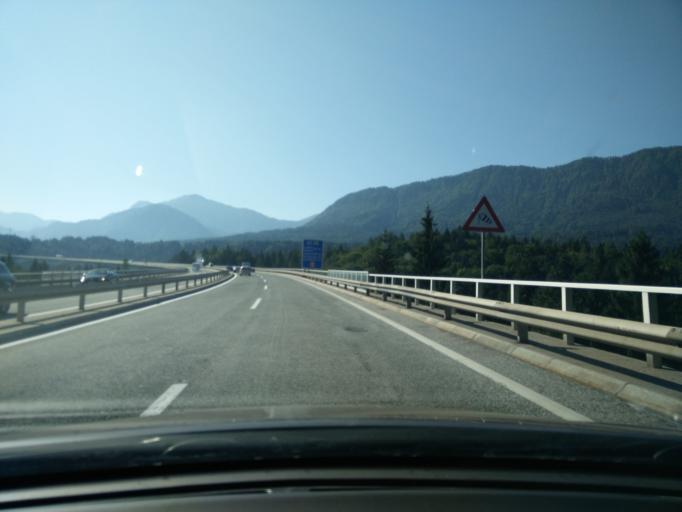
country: AT
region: Carinthia
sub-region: Politischer Bezirk Villach Land
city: Rosegg
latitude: 46.5549
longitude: 14.0062
